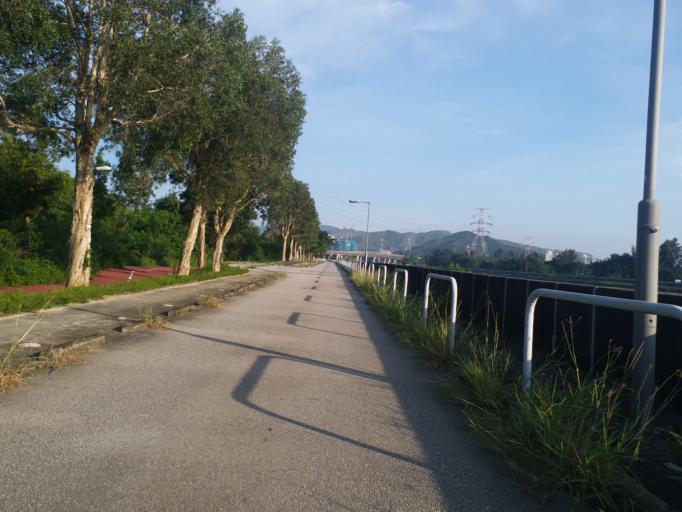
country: HK
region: Yuen Long
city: Yuen Long Kau Hui
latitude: 22.4595
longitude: 114.0469
